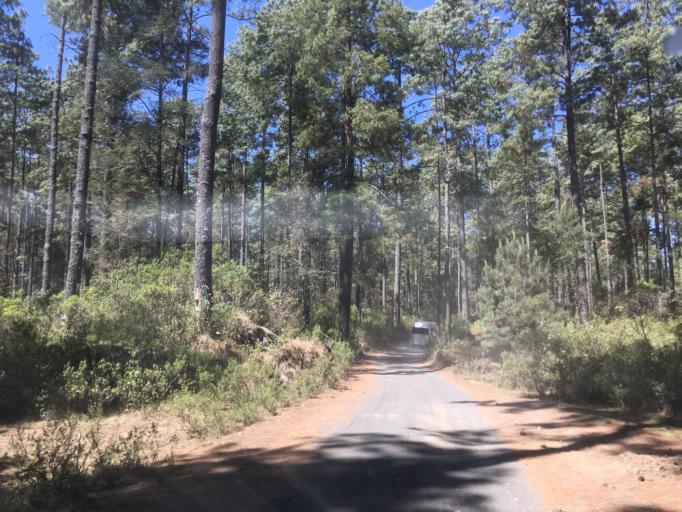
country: MX
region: Michoacan
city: Angahuan
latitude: 19.4641
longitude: -102.2172
